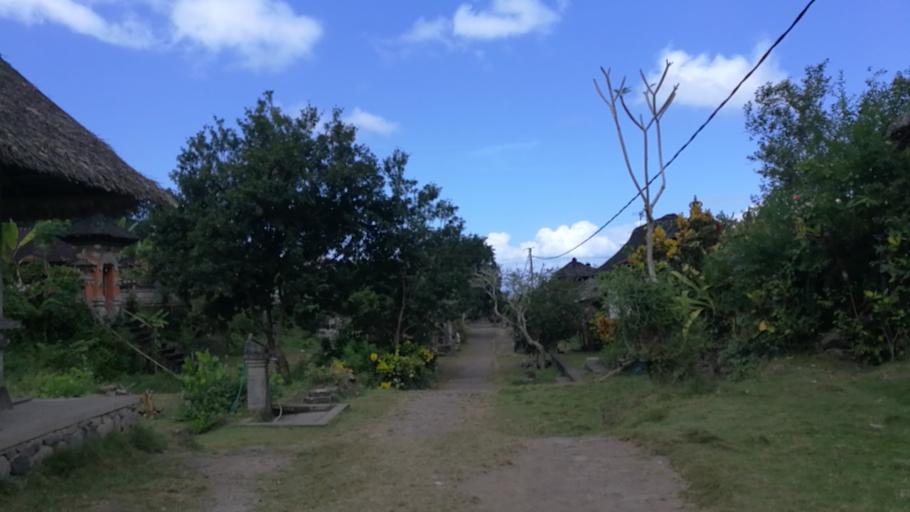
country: ID
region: Bali
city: Banjar Pegeringsingan
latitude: -8.4735
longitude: 115.5670
